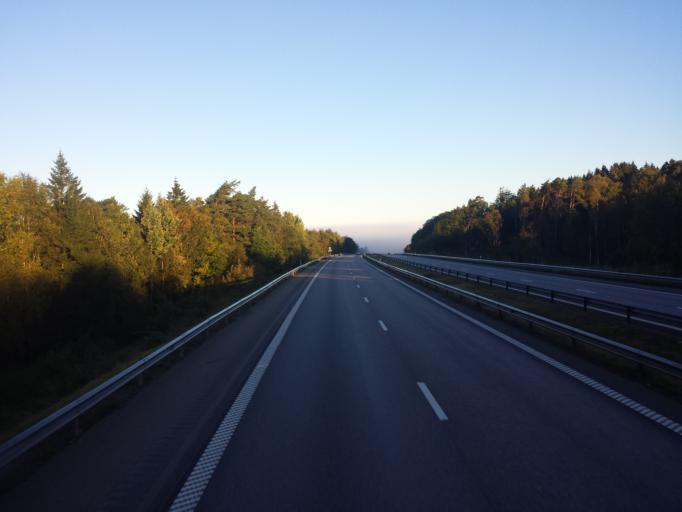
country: SE
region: Halland
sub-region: Kungsbacka Kommun
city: Kungsbacka
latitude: 57.4480
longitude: 12.1020
